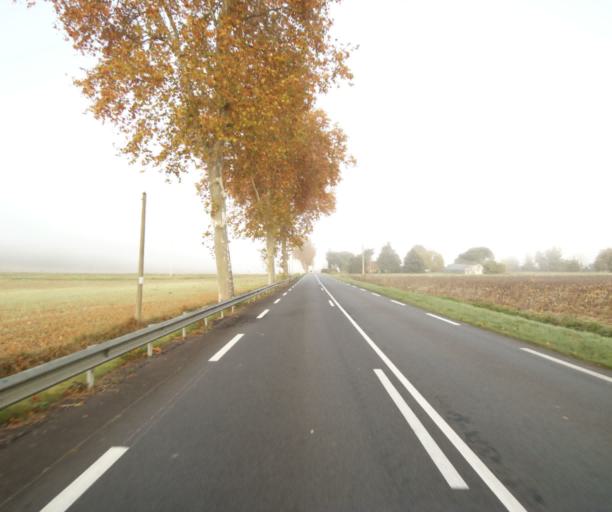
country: FR
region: Midi-Pyrenees
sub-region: Departement du Tarn-et-Garonne
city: Nohic
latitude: 43.9346
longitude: 1.4865
